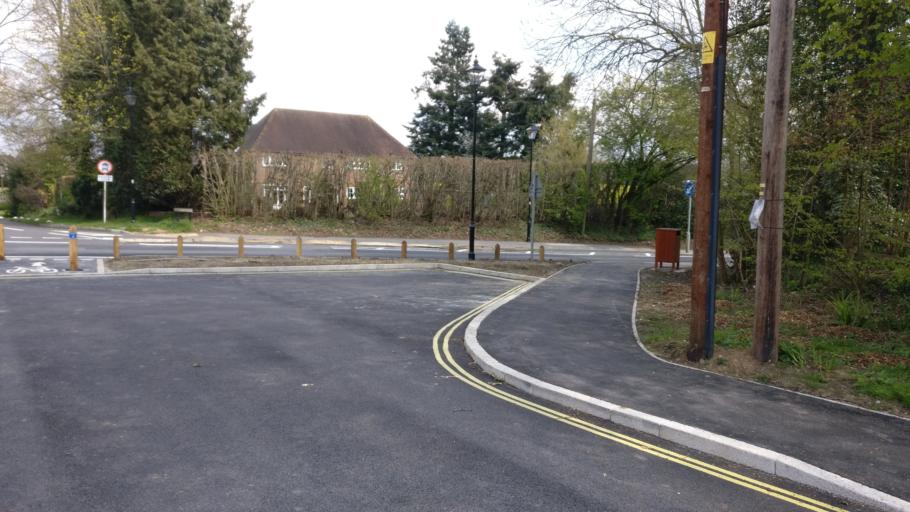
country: GB
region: England
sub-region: Hampshire
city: Eversley
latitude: 51.3025
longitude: -0.8984
